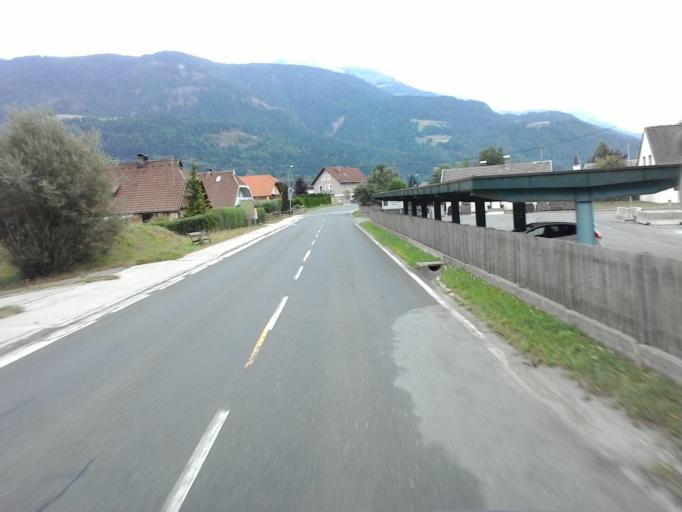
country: AT
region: Carinthia
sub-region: Politischer Bezirk Spittal an der Drau
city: Oberdrauburg
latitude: 46.6710
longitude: 12.9932
